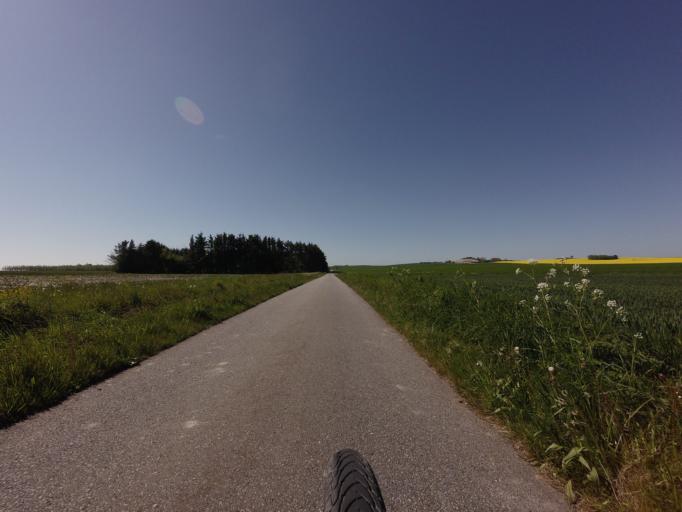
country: DK
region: North Denmark
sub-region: Hjorring Kommune
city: Vra
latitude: 57.3761
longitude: 9.8142
